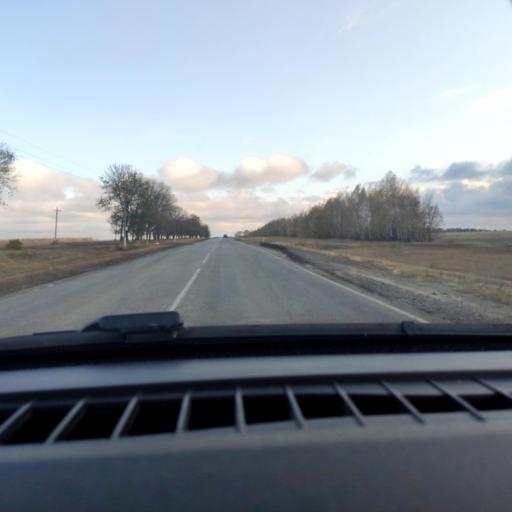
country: RU
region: Belgorod
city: Ilovka
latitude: 50.7131
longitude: 38.6627
